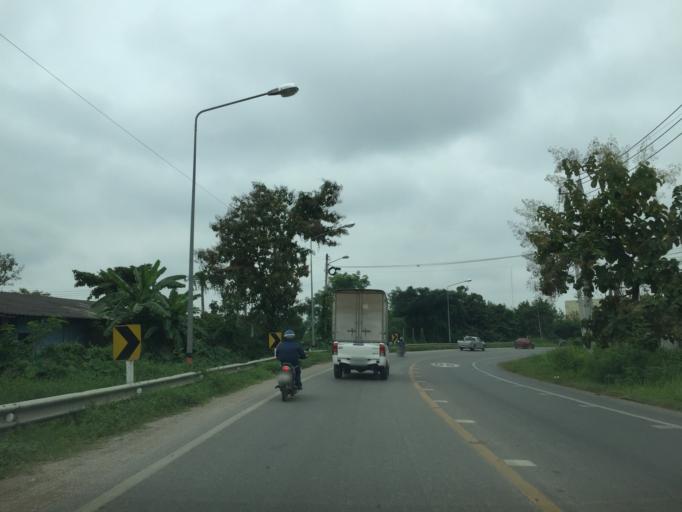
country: TH
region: Lamphun
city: Lamphun
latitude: 18.5828
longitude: 99.0591
